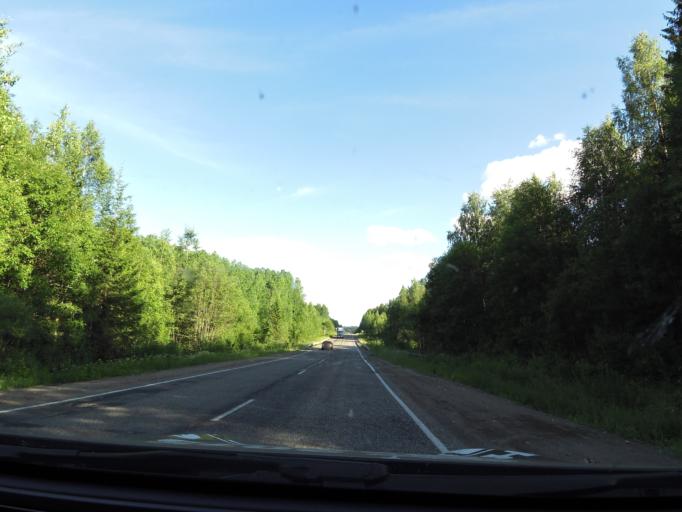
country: RU
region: Kirov
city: Omutninsk
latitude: 58.7444
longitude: 52.0641
